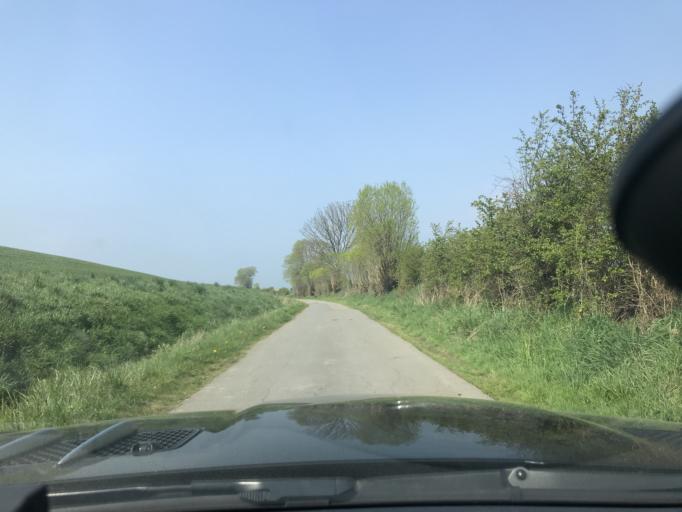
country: DE
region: Schleswig-Holstein
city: Gremersdorf
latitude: 54.3630
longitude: 10.9225
